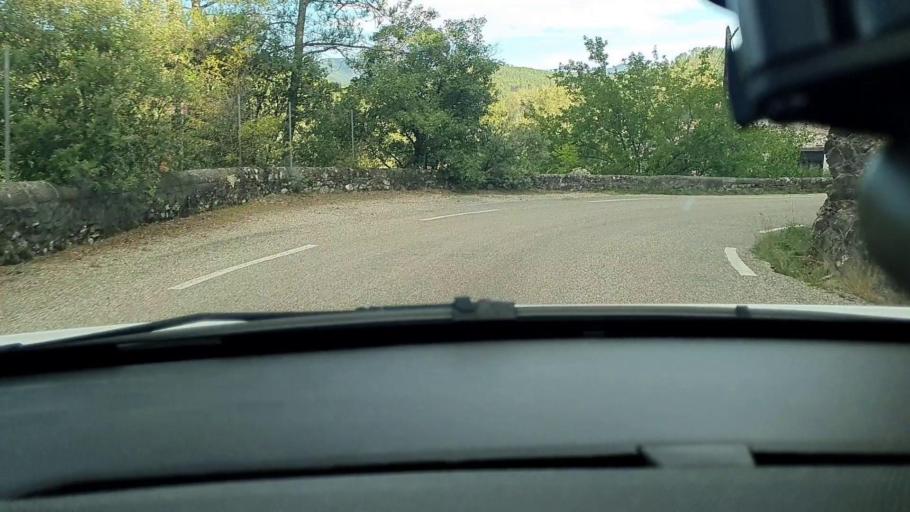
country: FR
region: Languedoc-Roussillon
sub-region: Departement du Gard
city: Besseges
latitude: 44.3230
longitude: 4.1193
